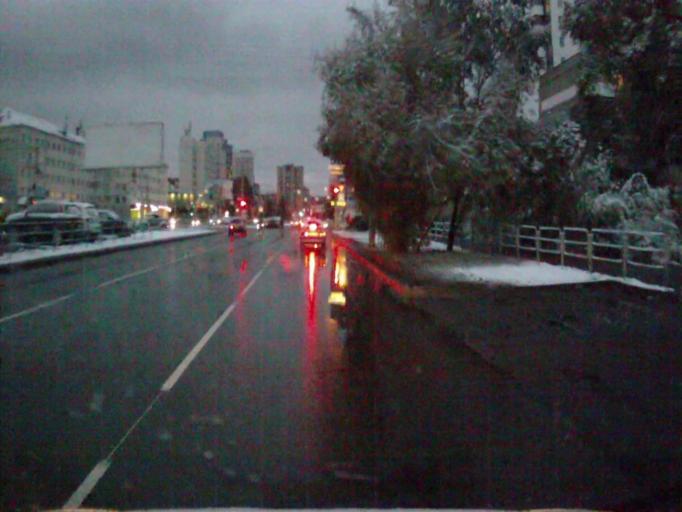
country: RU
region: Chelyabinsk
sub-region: Gorod Chelyabinsk
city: Chelyabinsk
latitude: 55.1494
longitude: 61.3913
